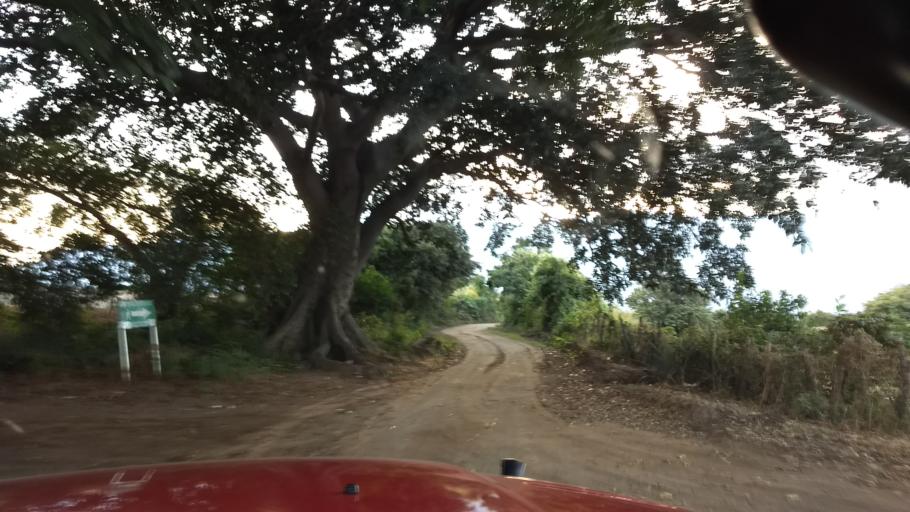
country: MX
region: Colima
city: Suchitlan
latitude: 19.4869
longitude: -103.7913
